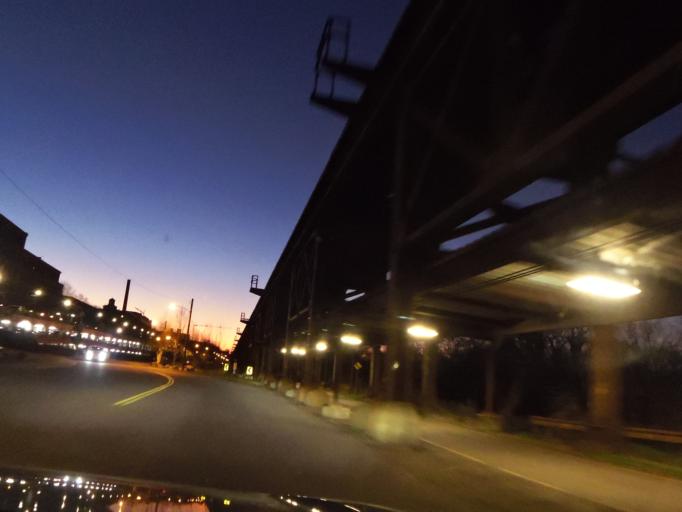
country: US
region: Virginia
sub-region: City of Richmond
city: Richmond
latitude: 37.5295
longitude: -77.4253
